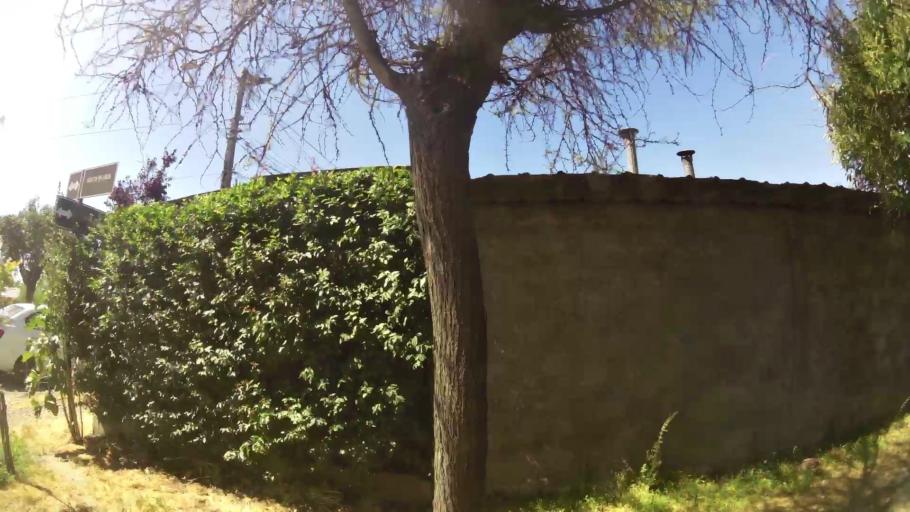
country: CL
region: Santiago Metropolitan
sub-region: Provincia de Maipo
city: San Bernardo
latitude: -33.5814
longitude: -70.6872
